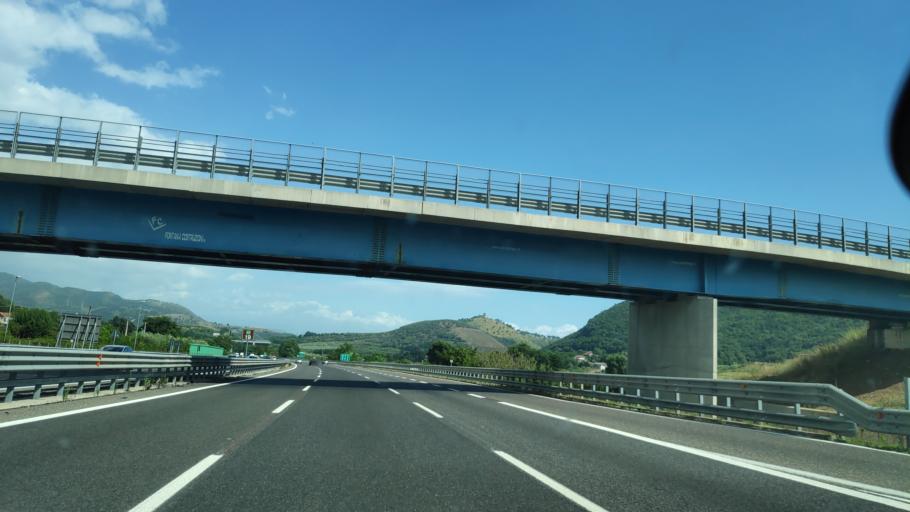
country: IT
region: Campania
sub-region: Provincia di Salerno
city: San Mango Piemonte
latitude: 40.6896
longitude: 14.8391
